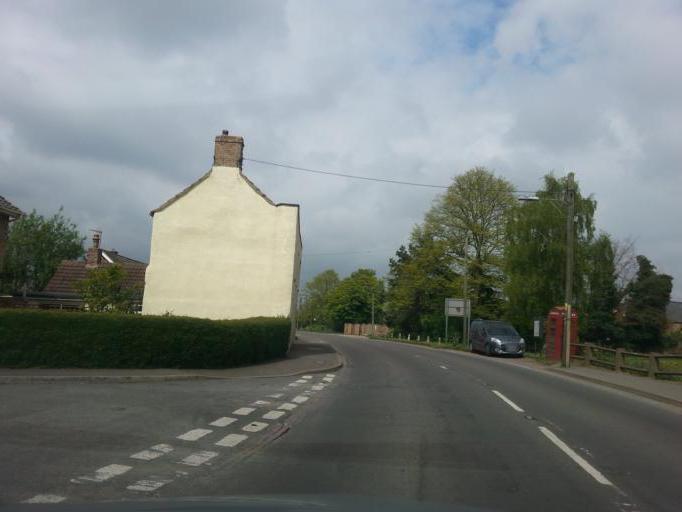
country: GB
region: England
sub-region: Norfolk
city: Outwell
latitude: 52.6102
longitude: 0.2328
